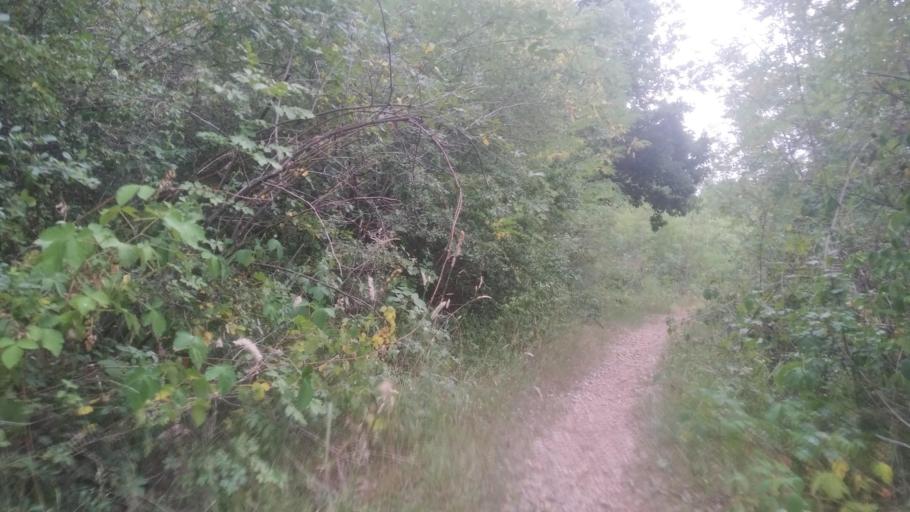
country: HU
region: Veszprem
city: Szentkiralyszabadja
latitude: 47.0014
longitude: 17.9738
